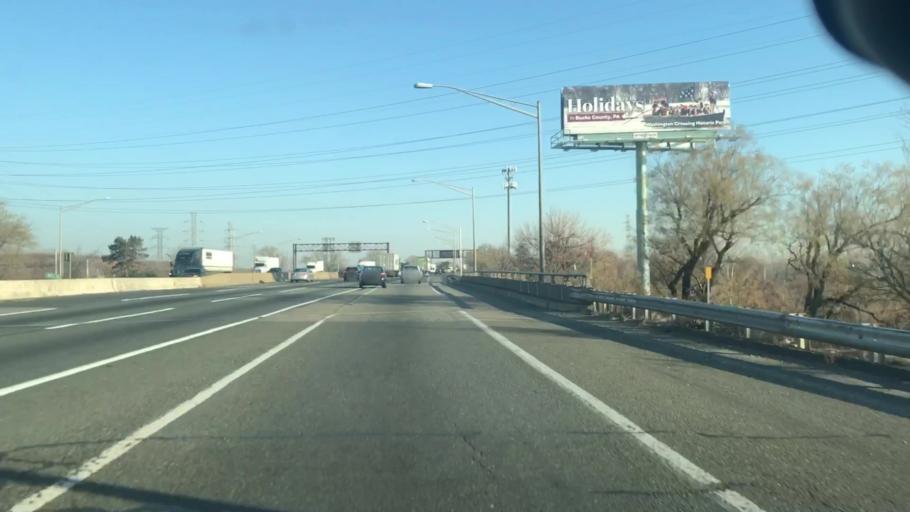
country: US
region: New Jersey
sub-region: Hudson County
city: Kearny
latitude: 40.7565
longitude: -74.1171
